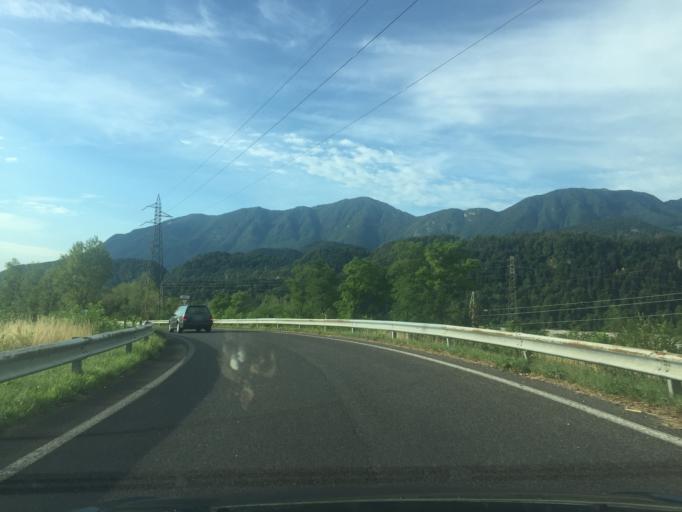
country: IT
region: Friuli Venezia Giulia
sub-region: Provincia di Udine
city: Chiaulis
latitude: 46.4001
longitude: 13.0026
